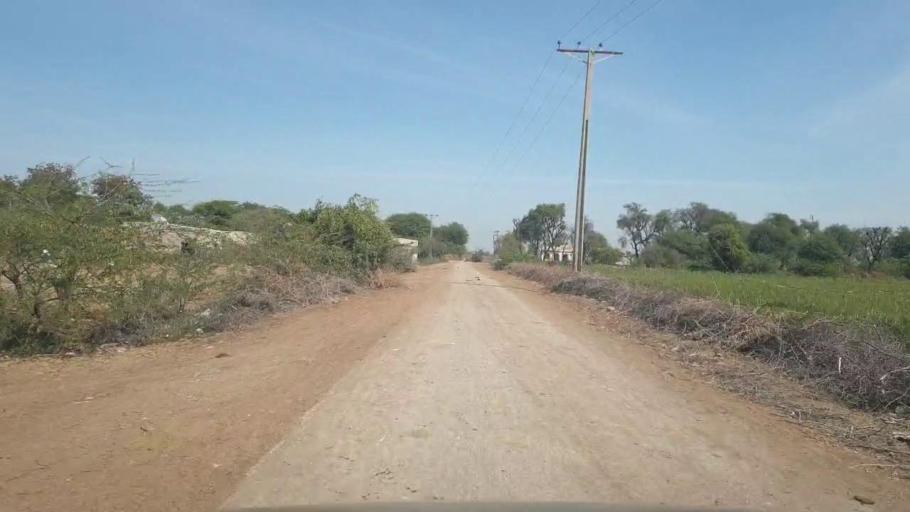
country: PK
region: Sindh
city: Umarkot
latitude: 25.3377
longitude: 69.6226
